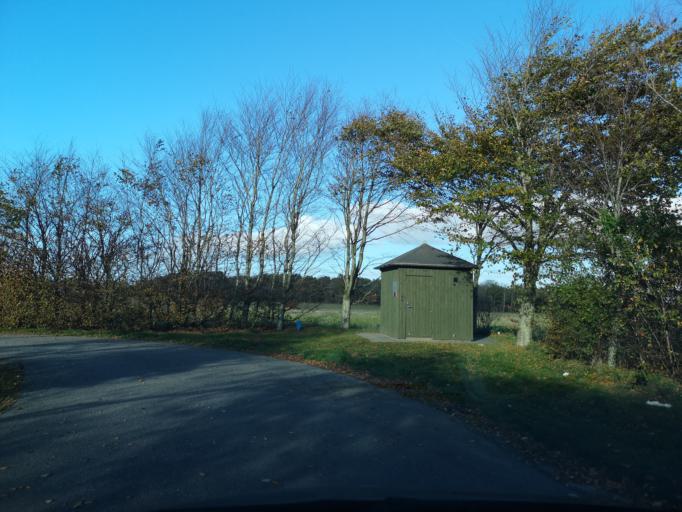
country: DK
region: South Denmark
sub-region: Varde Kommune
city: Varde
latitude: 55.7020
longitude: 8.4949
